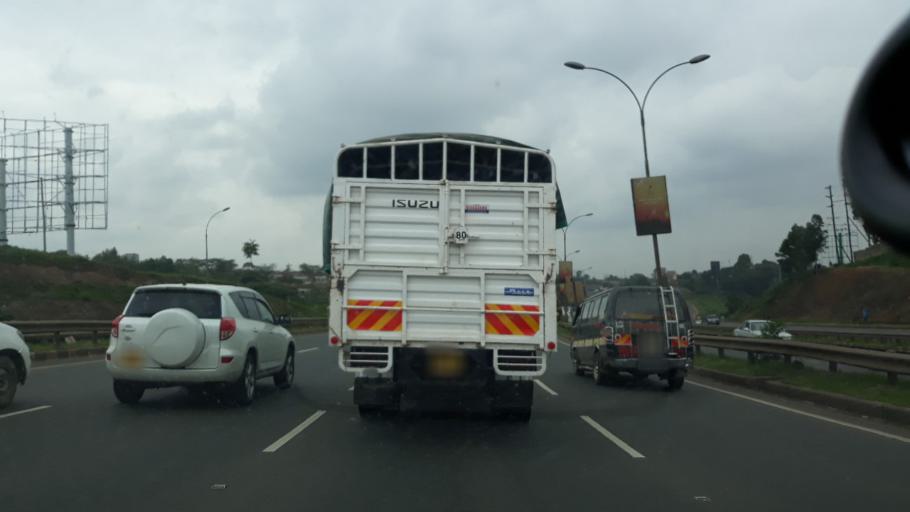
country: KE
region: Nairobi Area
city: Pumwani
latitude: -1.2583
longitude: 36.8472
